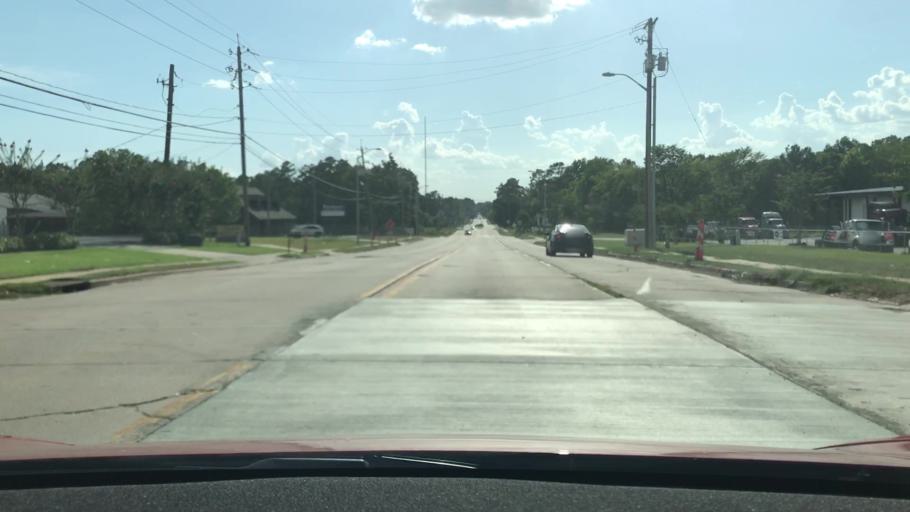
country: US
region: Louisiana
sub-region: Bossier Parish
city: Bossier City
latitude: 32.4130
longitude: -93.7681
